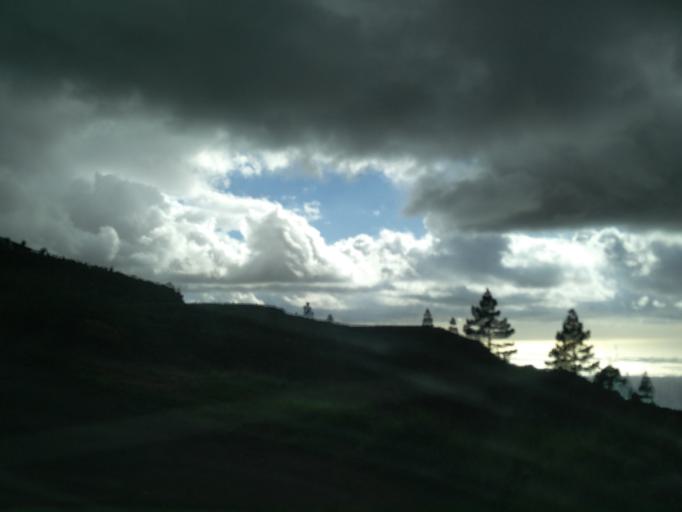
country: ES
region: Canary Islands
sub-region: Provincia de Santa Cruz de Tenerife
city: Arona
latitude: 28.1318
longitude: -16.6920
